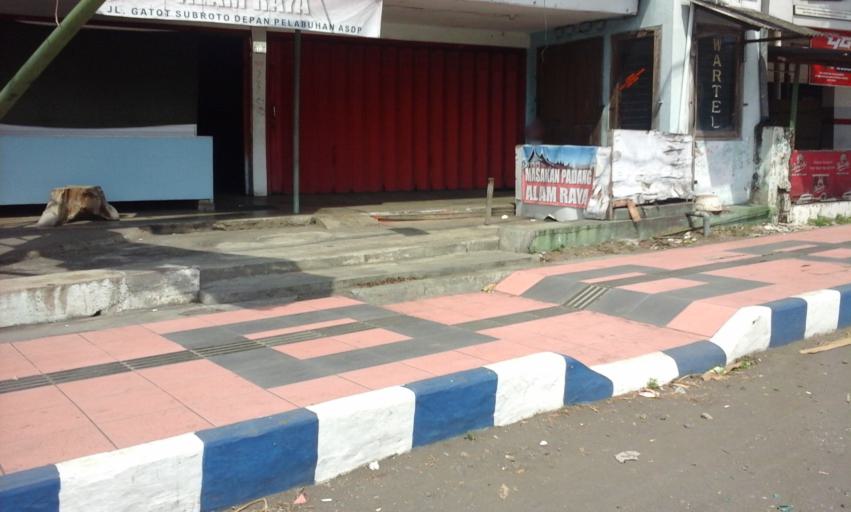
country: ID
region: East Java
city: Klatakan
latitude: -8.1440
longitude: 114.3997
